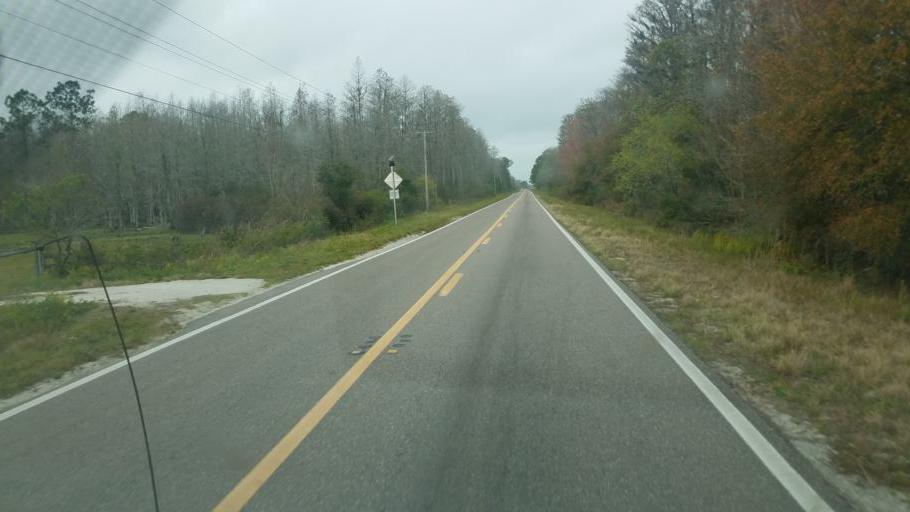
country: US
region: Florida
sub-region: Polk County
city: Polk City
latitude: 28.2585
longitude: -81.8282
